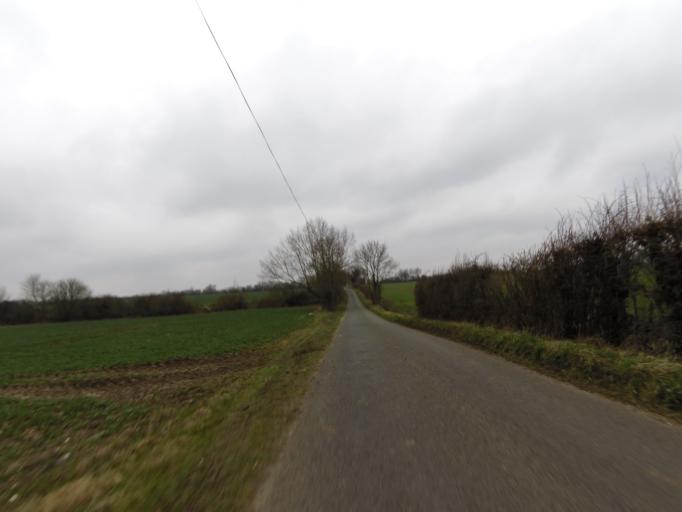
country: GB
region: England
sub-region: Suffolk
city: Framlingham
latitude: 52.2199
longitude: 1.3266
